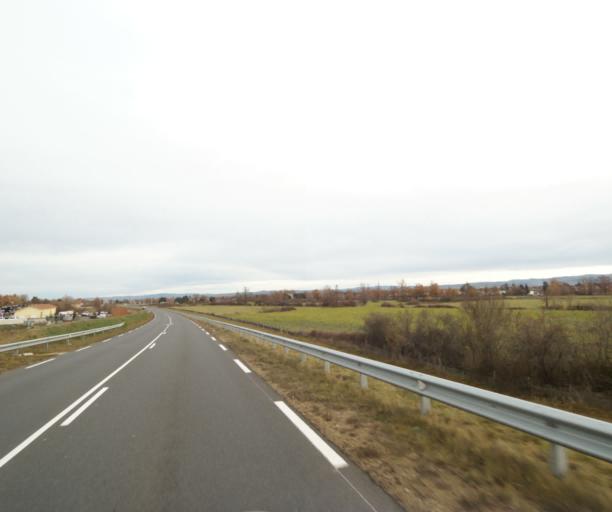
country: FR
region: Rhone-Alpes
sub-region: Departement de la Loire
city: Sury-le-Comtal
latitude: 45.5256
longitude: 4.1955
